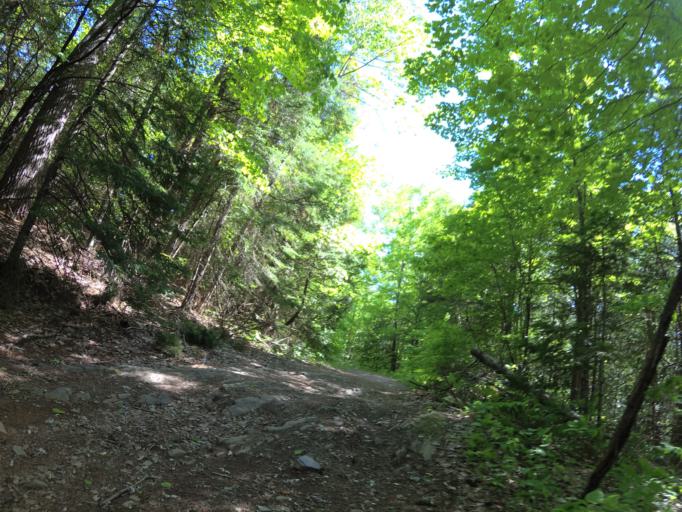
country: CA
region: Ontario
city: Renfrew
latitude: 45.0469
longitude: -76.8310
